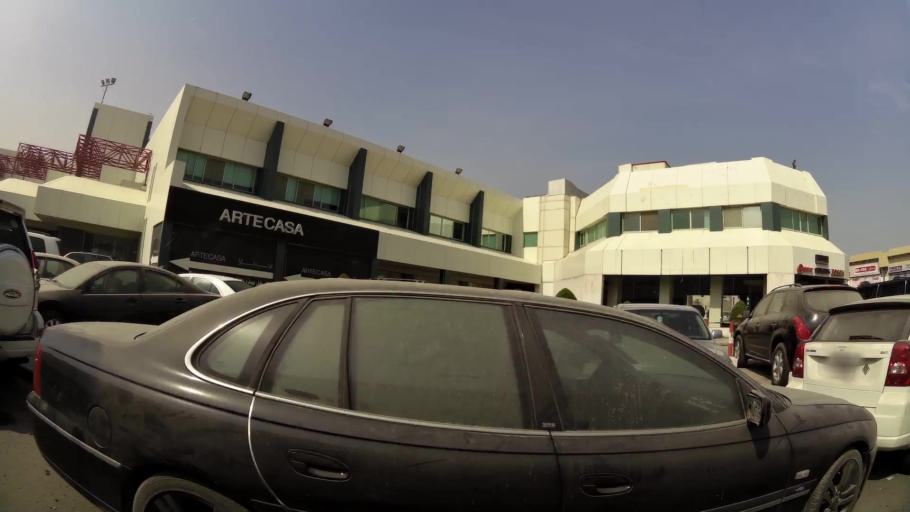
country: KW
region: Al Asimah
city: Ash Shamiyah
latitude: 29.3307
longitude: 47.9440
